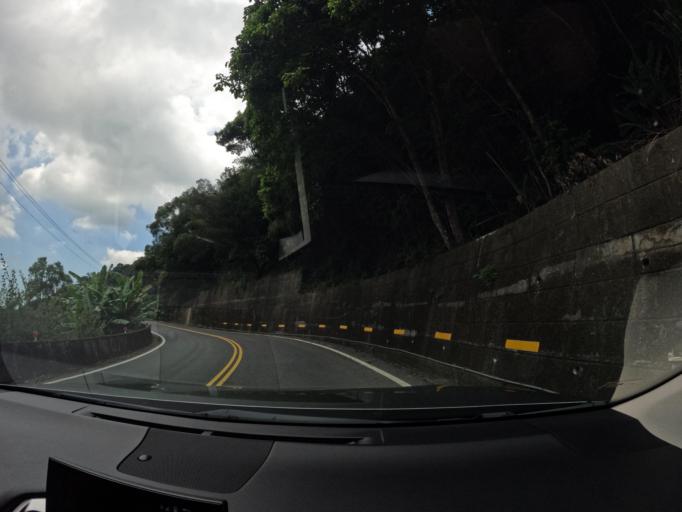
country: TW
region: Taiwan
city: Fengyuan
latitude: 24.3826
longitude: 120.8159
